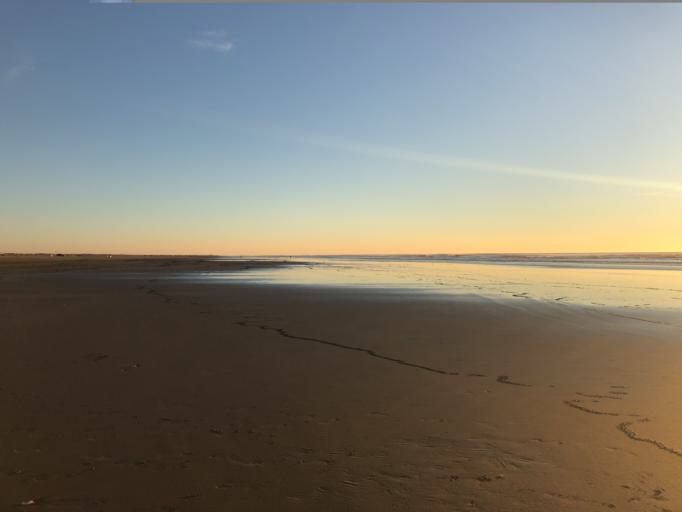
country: US
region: Washington
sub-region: Grays Harbor County
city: Ocean Shores
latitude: 47.0194
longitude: -124.1765
